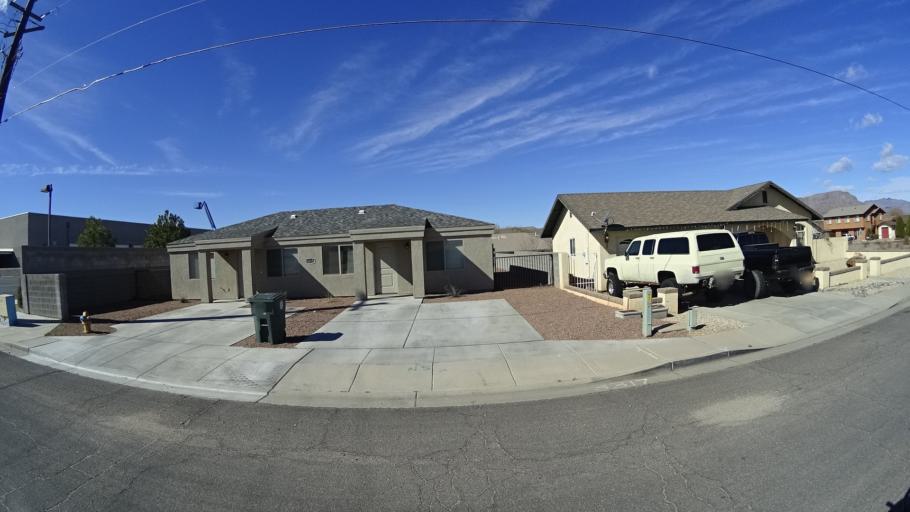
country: US
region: Arizona
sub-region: Mohave County
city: Kingman
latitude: 35.2196
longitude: -114.0203
